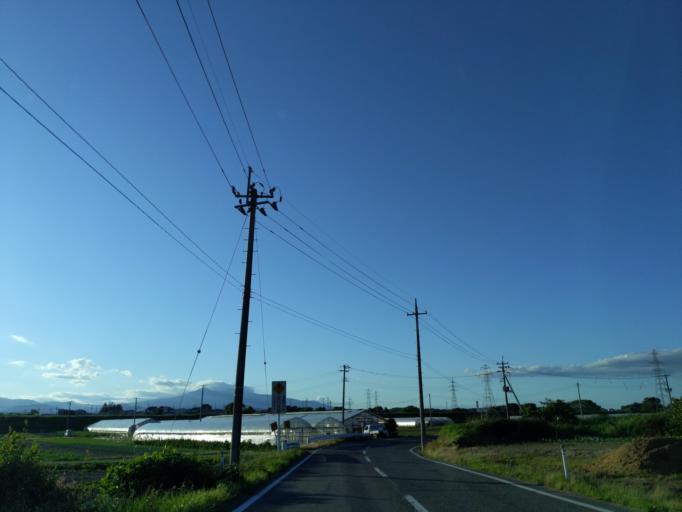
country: JP
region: Fukushima
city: Koriyama
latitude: 37.4115
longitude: 140.4123
